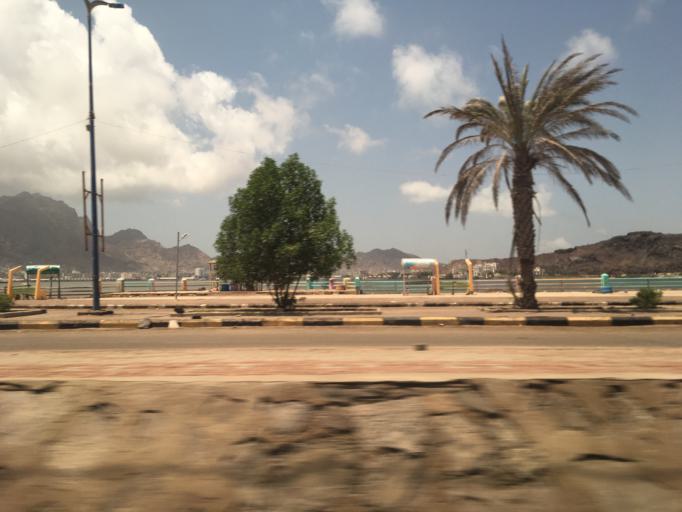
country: YE
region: Aden
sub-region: Khur Maksar
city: Khawr Maksar
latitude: 12.8076
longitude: 45.0262
